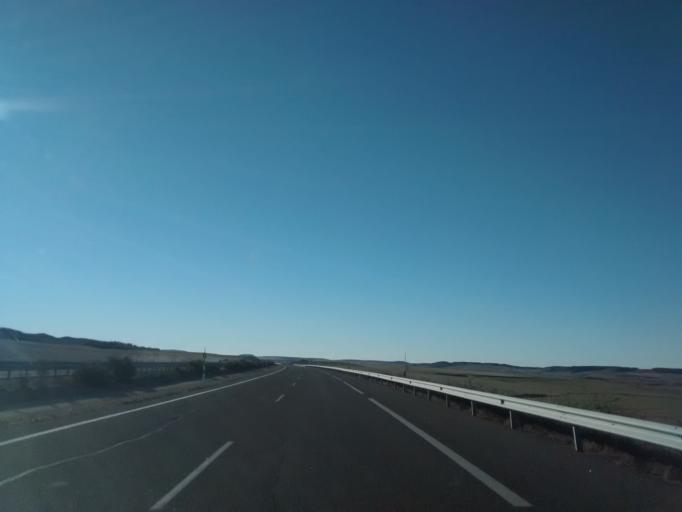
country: ES
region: Castille and Leon
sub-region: Provincia de Palencia
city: Pradanos de Ojeda
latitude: 42.6482
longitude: -4.3508
